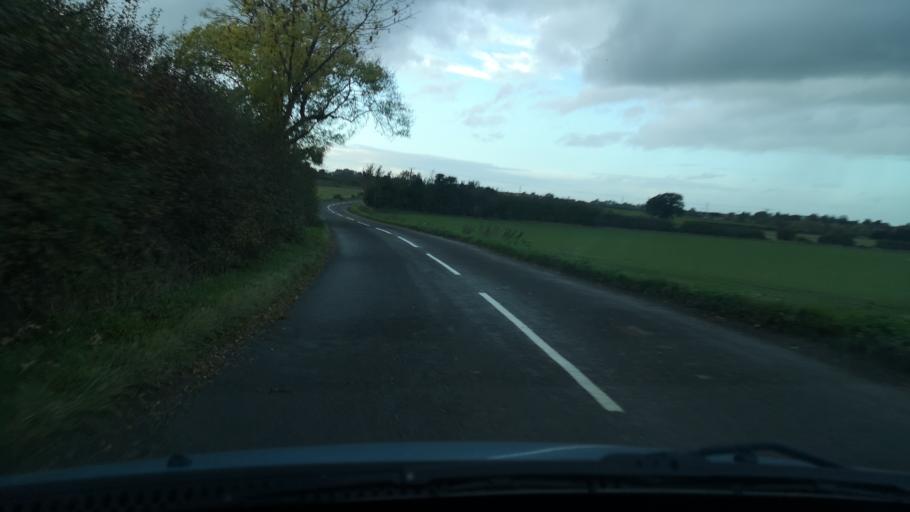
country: GB
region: England
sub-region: Doncaster
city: Norton
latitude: 53.6349
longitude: -1.2028
